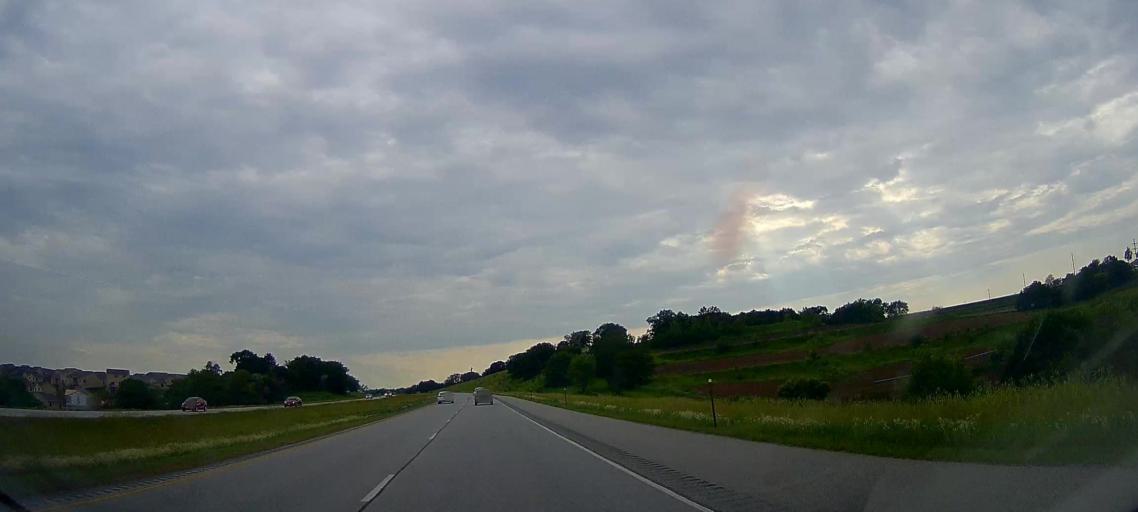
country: US
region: Nebraska
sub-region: Douglas County
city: Bennington
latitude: 41.3323
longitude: -96.0528
